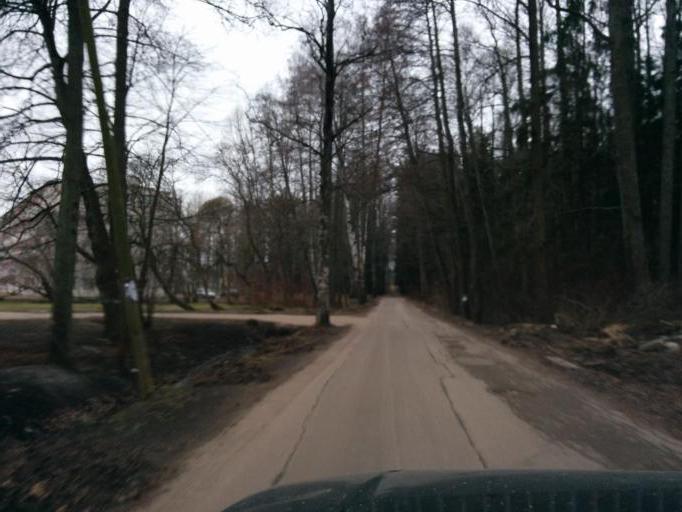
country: LV
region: Babite
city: Pinki
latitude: 56.9734
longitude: 23.8477
